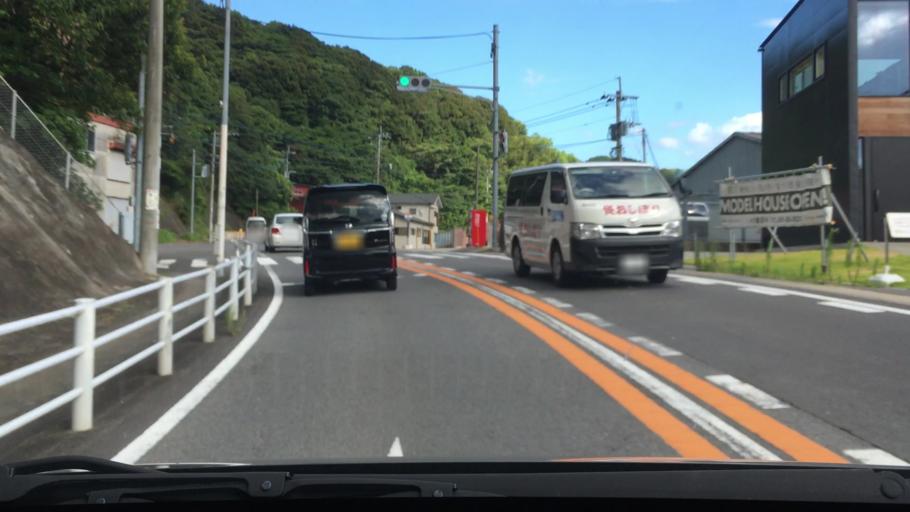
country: JP
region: Nagasaki
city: Togitsu
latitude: 32.8117
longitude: 129.8092
